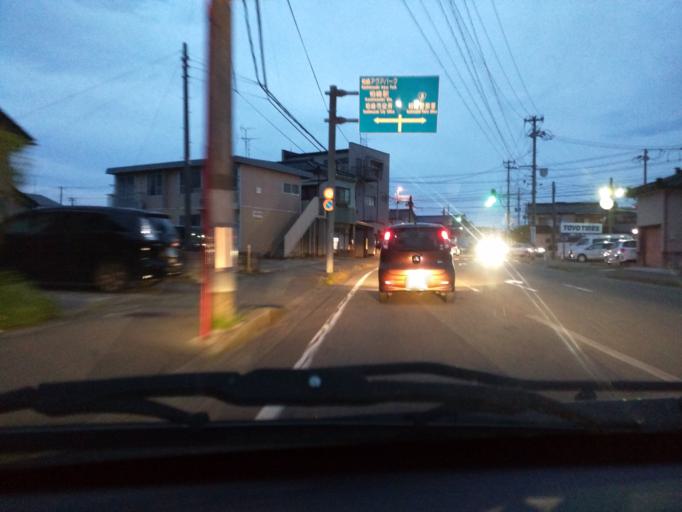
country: JP
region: Niigata
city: Kashiwazaki
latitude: 37.3692
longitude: 138.5735
